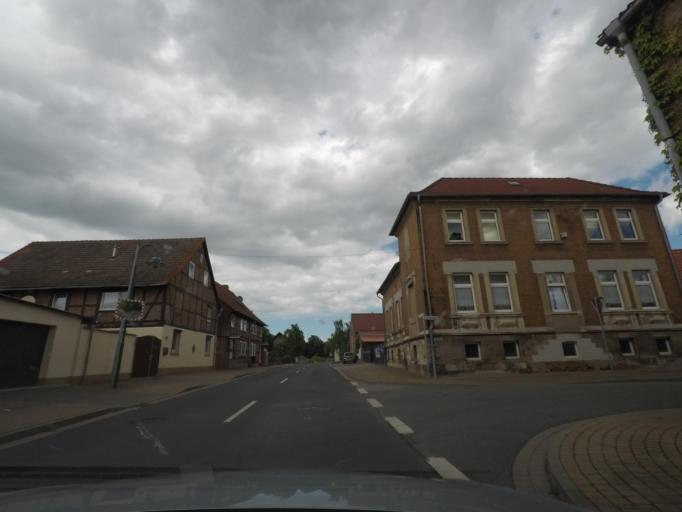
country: DE
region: Saxony-Anhalt
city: Ausleben
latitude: 52.0656
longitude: 11.0803
